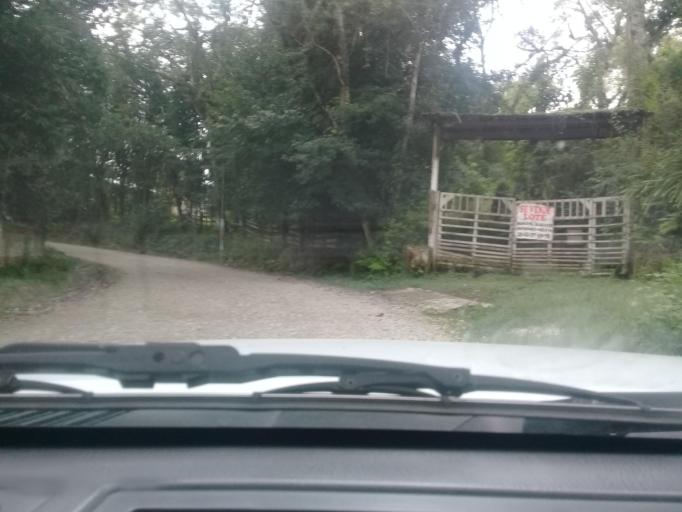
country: MX
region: Veracruz
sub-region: Tlalnelhuayocan
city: Otilpan
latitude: 19.5484
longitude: -96.9740
